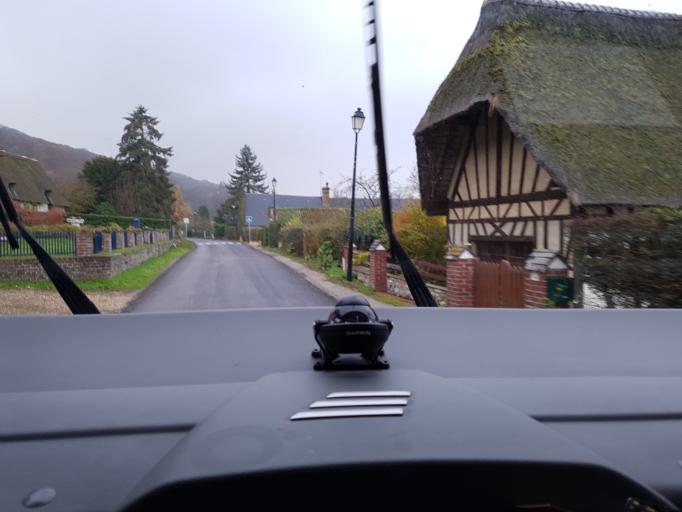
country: FR
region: Haute-Normandie
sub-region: Departement de la Seine-Maritime
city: Petiville
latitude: 49.4260
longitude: 0.6073
